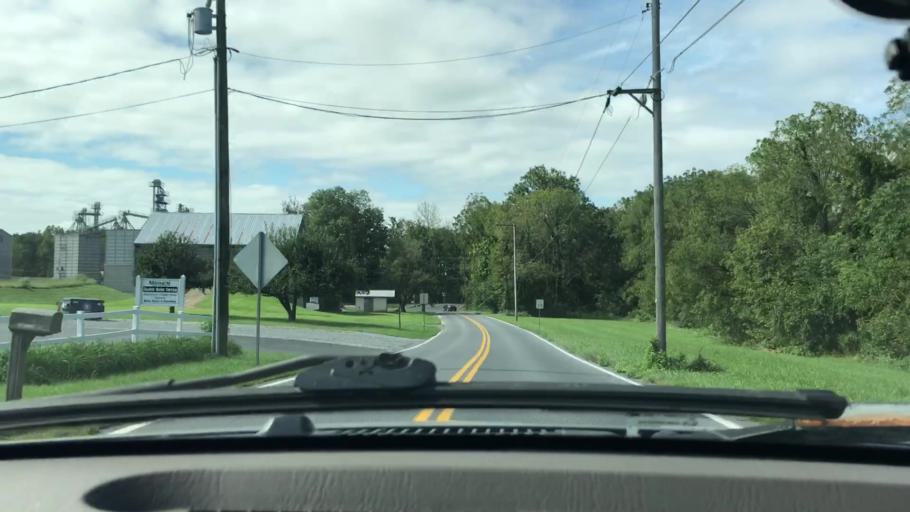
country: US
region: Pennsylvania
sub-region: Lancaster County
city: Manheim
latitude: 40.1432
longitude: -76.4066
